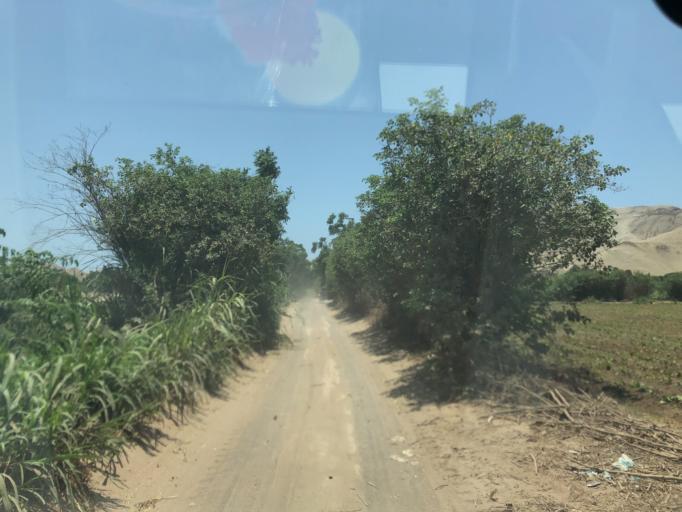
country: PE
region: Lima
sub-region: Provincia de Canete
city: Quilmana
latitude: -13.0015
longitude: -76.4481
